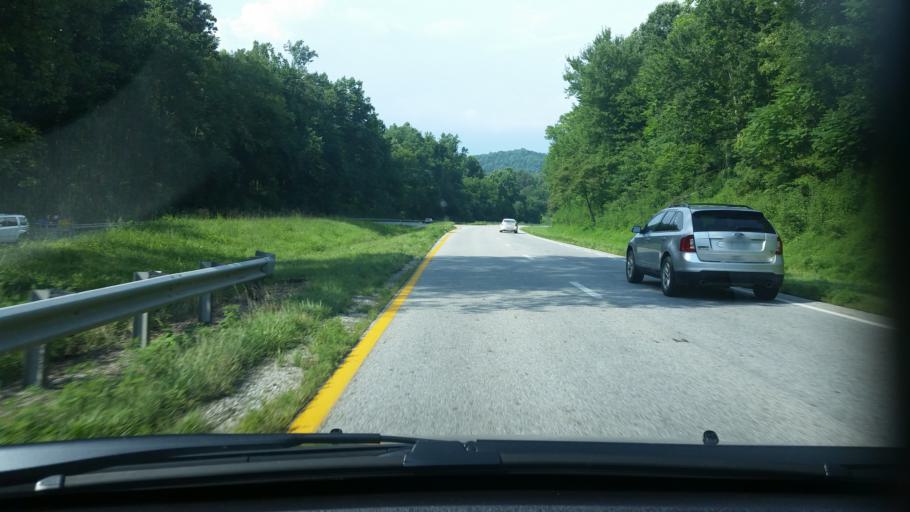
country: US
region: Virginia
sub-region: Nelson County
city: Lovingston
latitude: 37.7369
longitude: -78.8917
